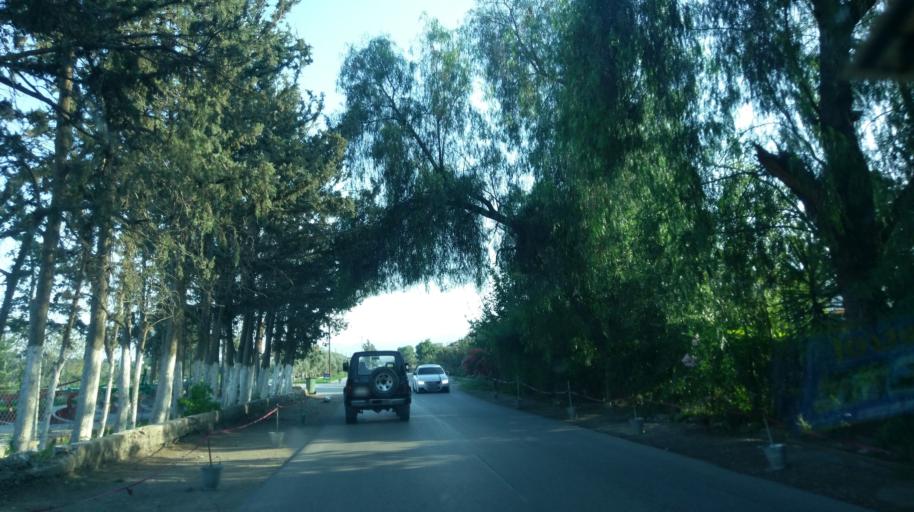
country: CY
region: Lefkosia
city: Lefka
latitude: 35.1613
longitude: 32.9016
